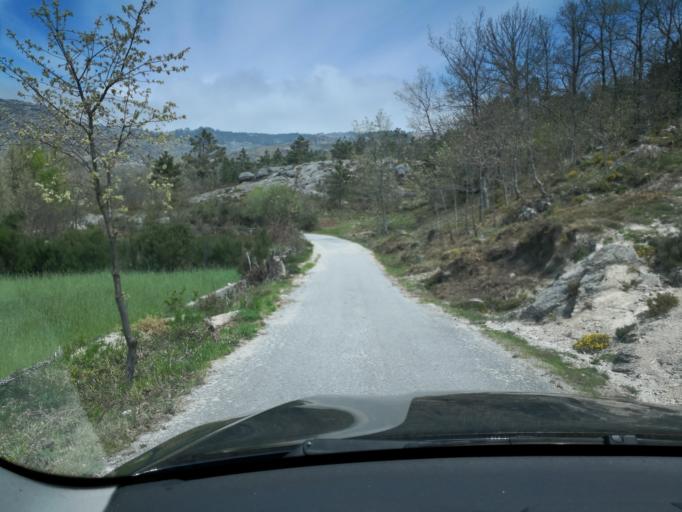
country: PT
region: Vila Real
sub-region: Vila Real
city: Vila Real
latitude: 41.3289
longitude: -7.8003
